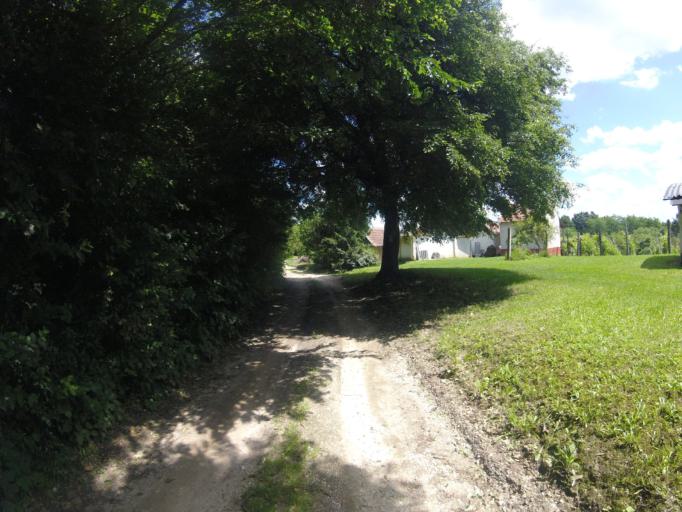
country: HU
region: Zala
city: Zalalovo
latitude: 46.8331
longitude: 16.5605
